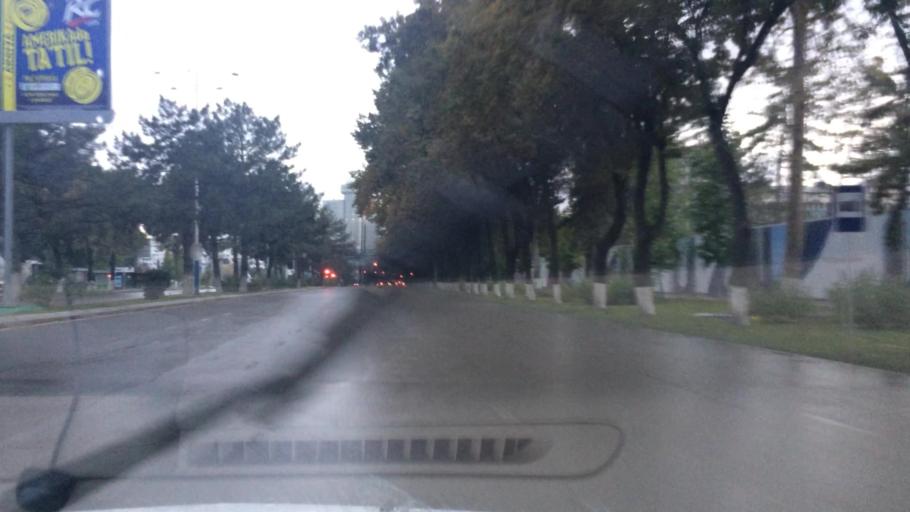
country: UZ
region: Toshkent Shahri
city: Tashkent
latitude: 41.3118
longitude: 69.2456
